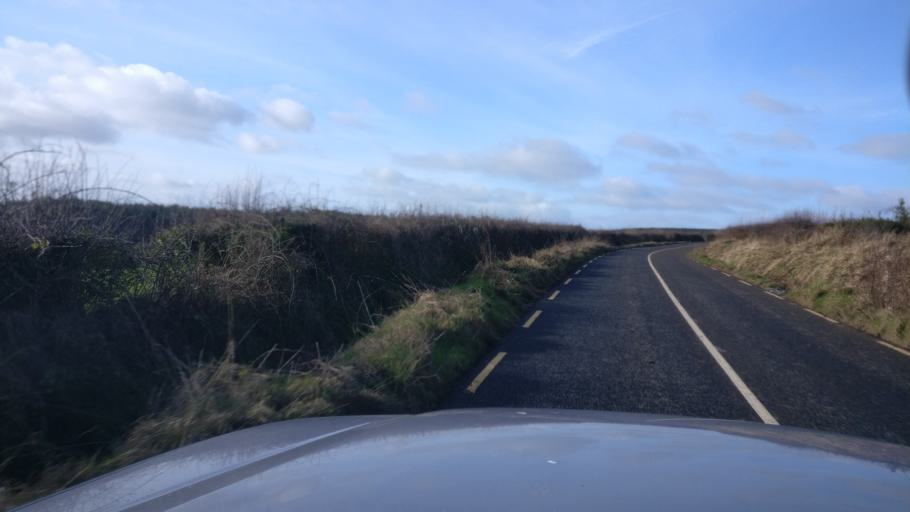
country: IE
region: Leinster
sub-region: Kilkenny
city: Castlecomer
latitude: 52.9037
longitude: -7.1794
